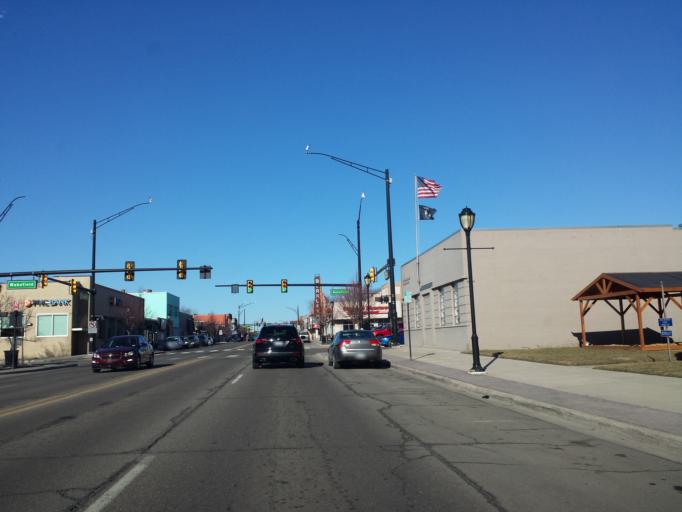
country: US
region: Michigan
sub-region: Oakland County
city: Berkley
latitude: 42.5032
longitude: -83.1876
